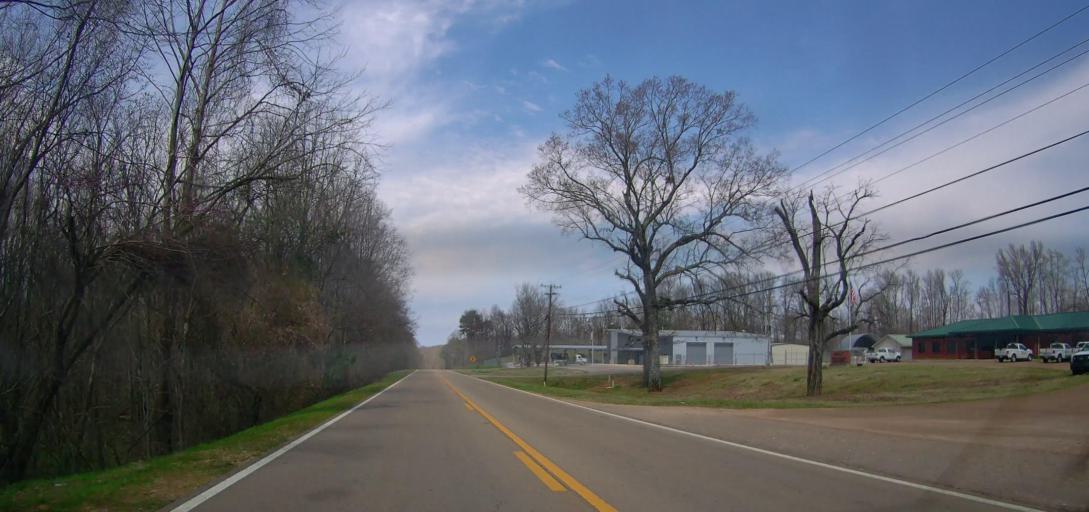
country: US
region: Mississippi
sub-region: Union County
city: New Albany
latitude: 34.4599
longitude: -88.9782
